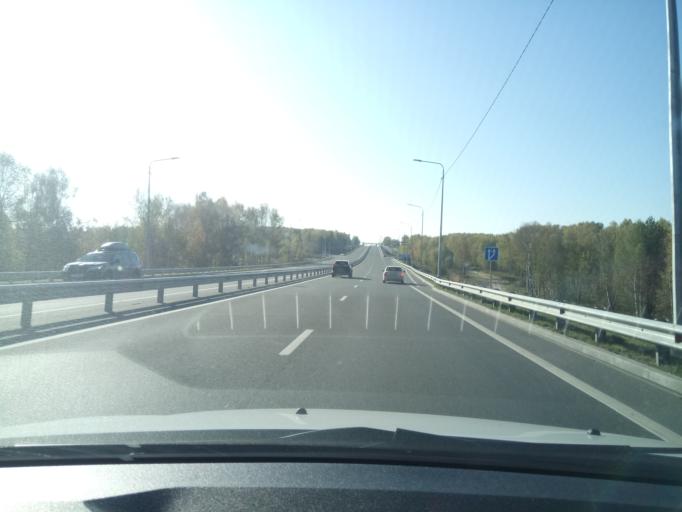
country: RU
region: Nizjnij Novgorod
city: Burevestnik
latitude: 56.0091
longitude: 43.9658
